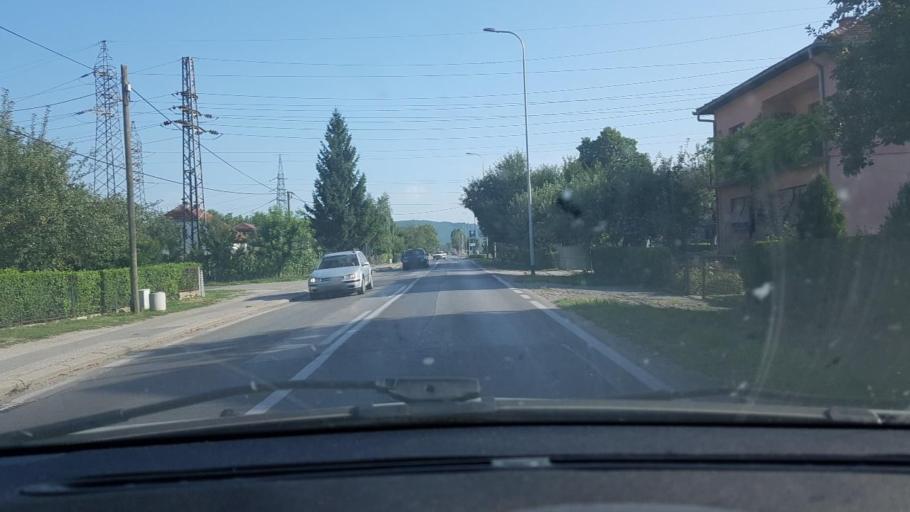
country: BA
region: Federation of Bosnia and Herzegovina
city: Bihac
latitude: 44.8281
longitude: 15.8818
